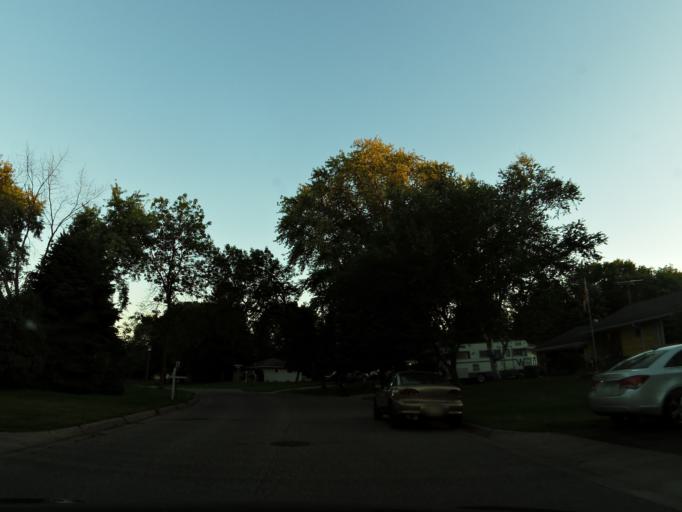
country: US
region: Minnesota
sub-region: Washington County
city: Oakdale
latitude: 44.9696
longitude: -92.9679
